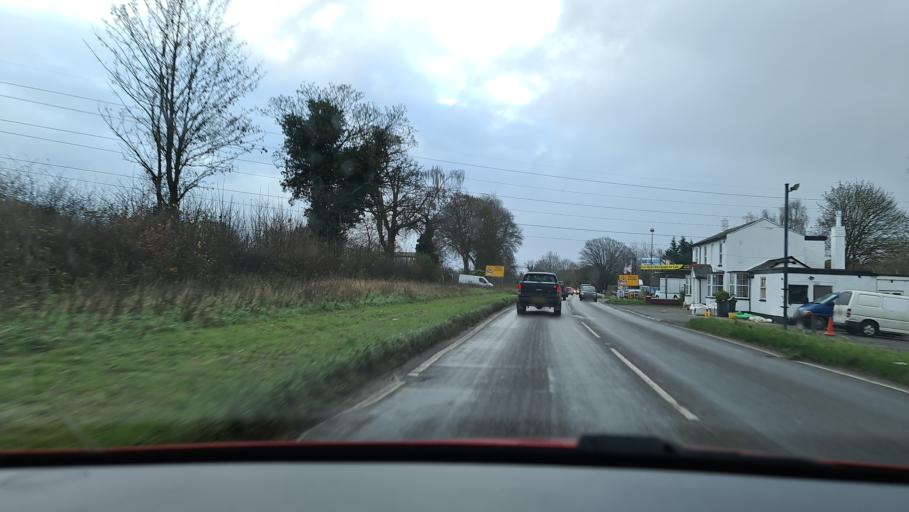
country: GB
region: England
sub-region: Buckinghamshire
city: Great Missenden
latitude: 51.6861
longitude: -0.6847
